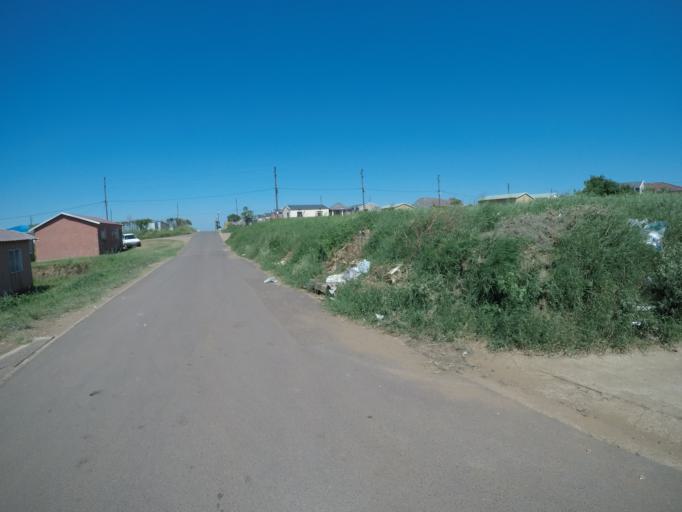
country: ZA
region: KwaZulu-Natal
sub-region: uThungulu District Municipality
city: Empangeni
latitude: -28.7679
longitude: 31.8786
